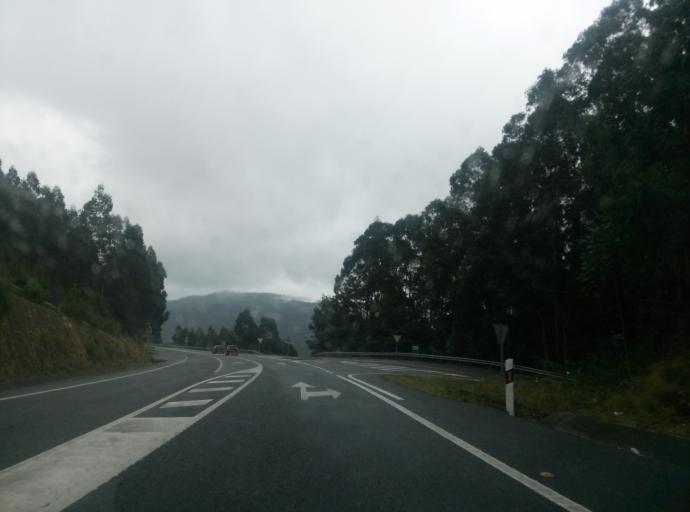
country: ES
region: Galicia
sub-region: Provincia de Lugo
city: Viveiro
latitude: 43.5916
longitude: -7.6223
